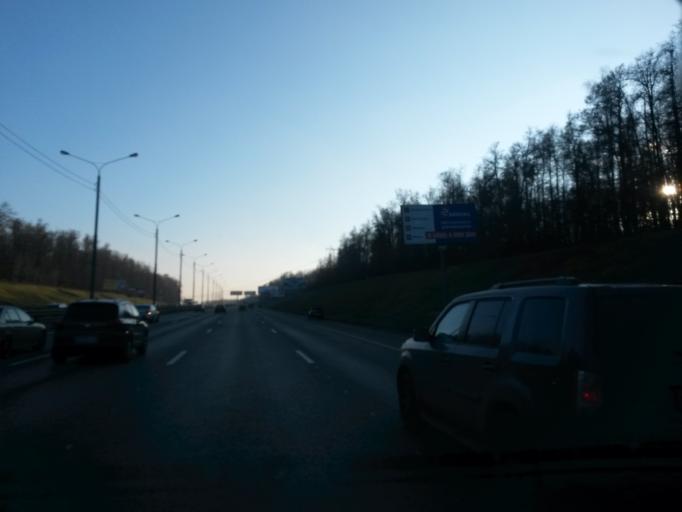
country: RU
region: Moscow
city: Annino
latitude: 55.5520
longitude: 37.6056
